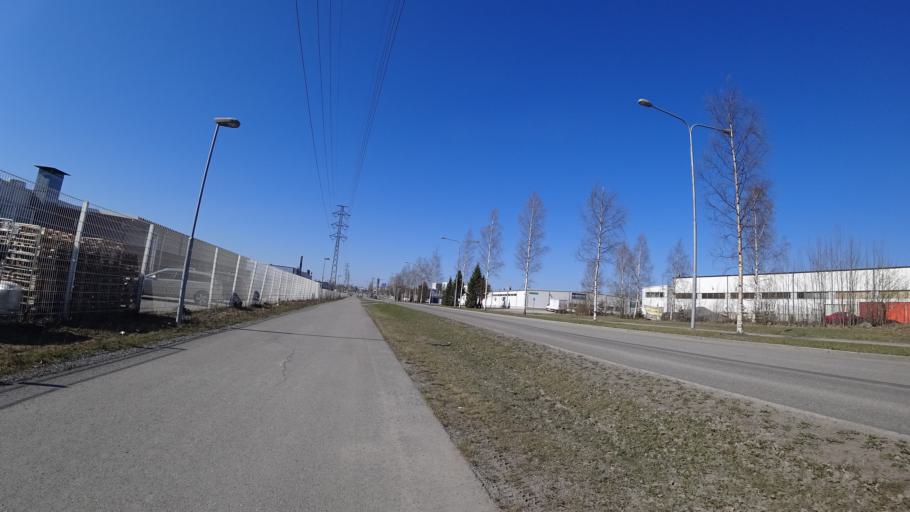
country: FI
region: Pirkanmaa
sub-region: Tampere
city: Pirkkala
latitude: 61.5150
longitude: 23.6721
